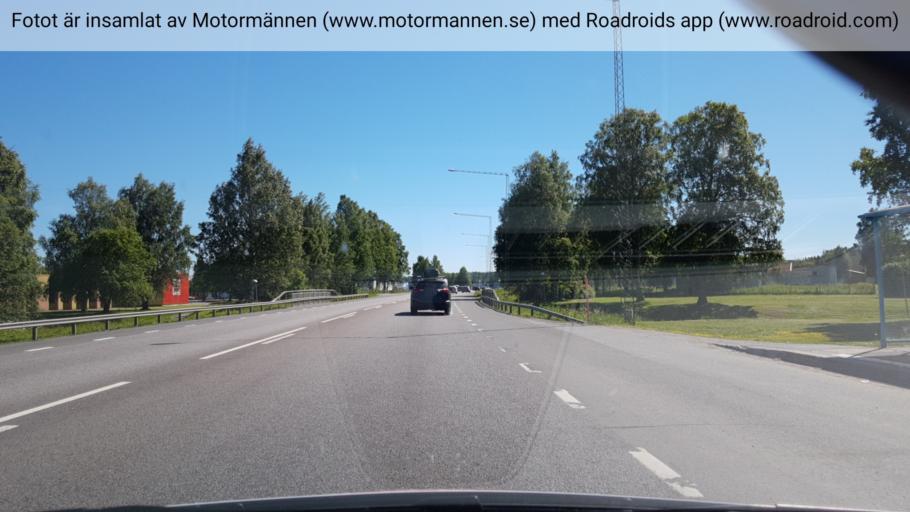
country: SE
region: Vaesterbotten
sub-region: Skelleftea Kommun
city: Skelleftea
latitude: 64.7418
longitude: 20.9621
